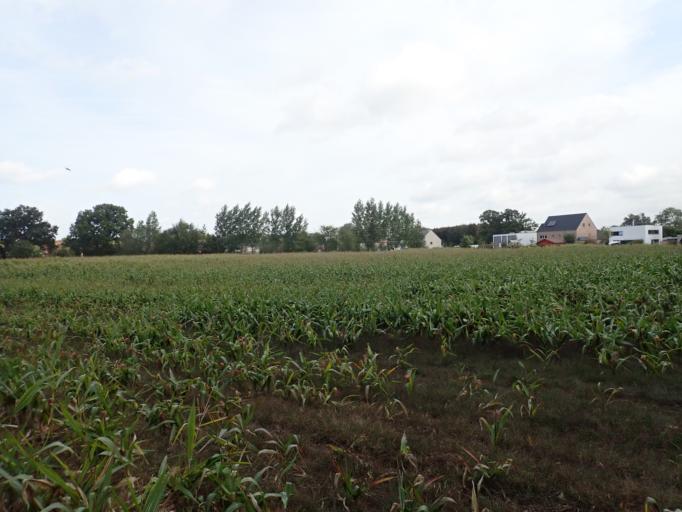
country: BE
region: Flanders
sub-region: Provincie Antwerpen
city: Lille
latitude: 51.2262
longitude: 4.8267
